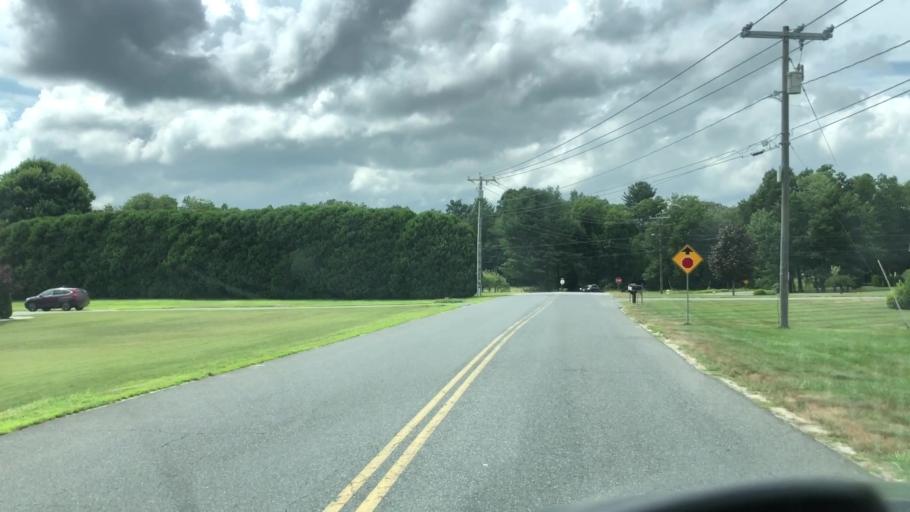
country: US
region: Massachusetts
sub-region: Hampshire County
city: Easthampton
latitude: 42.2375
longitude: -72.6901
